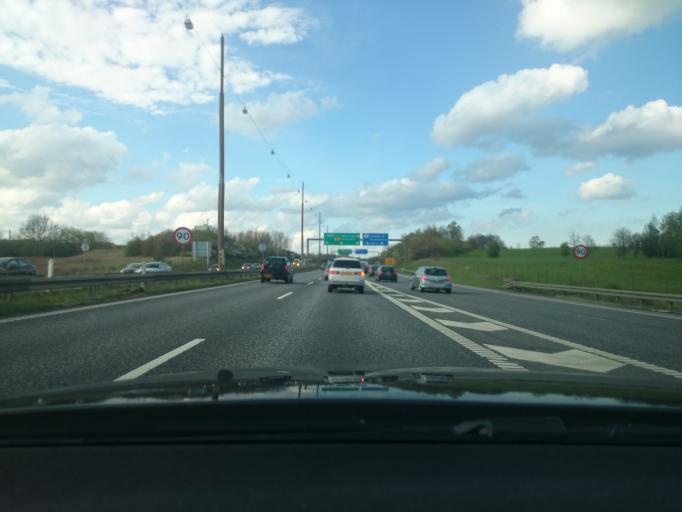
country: DK
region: Capital Region
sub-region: Lyngby-Tarbaek Kommune
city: Kongens Lyngby
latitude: 55.7703
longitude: 12.5237
